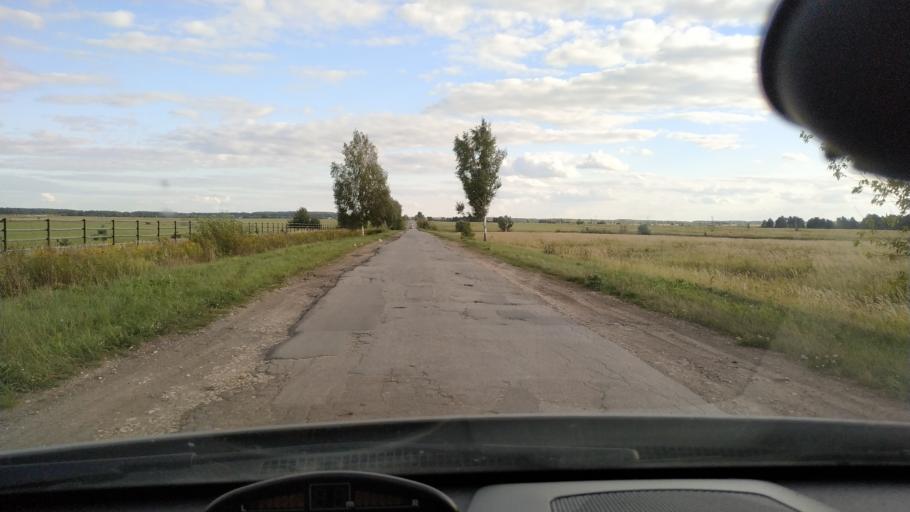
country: RU
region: Rjazan
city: Polyany
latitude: 54.5756
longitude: 39.8611
